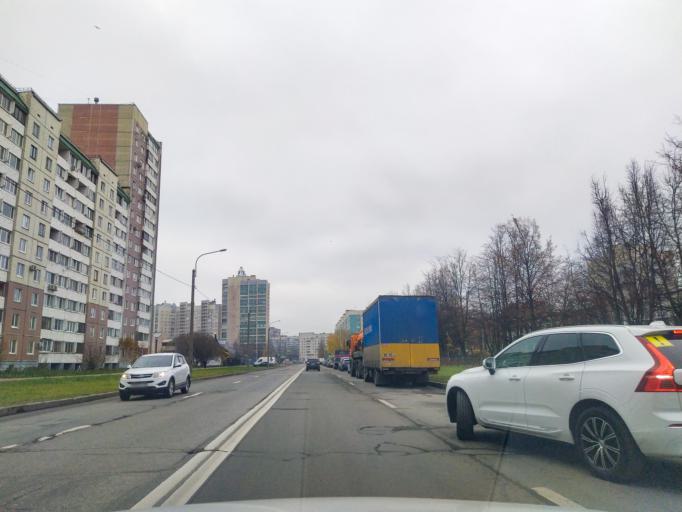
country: RU
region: St.-Petersburg
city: Ozerki
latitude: 60.0352
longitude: 30.3346
